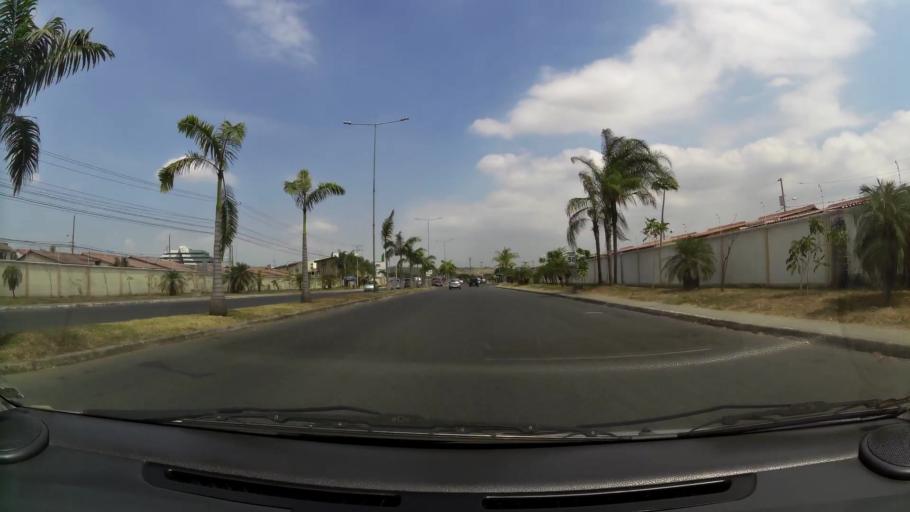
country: EC
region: Guayas
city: El Triunfo
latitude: -2.0479
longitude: -79.9151
